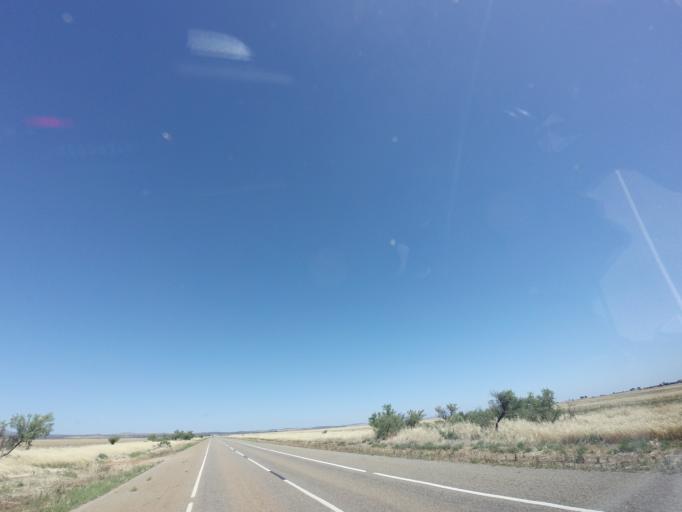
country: AU
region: South Australia
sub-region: Peterborough
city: Peterborough
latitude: -32.8218
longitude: 138.6981
